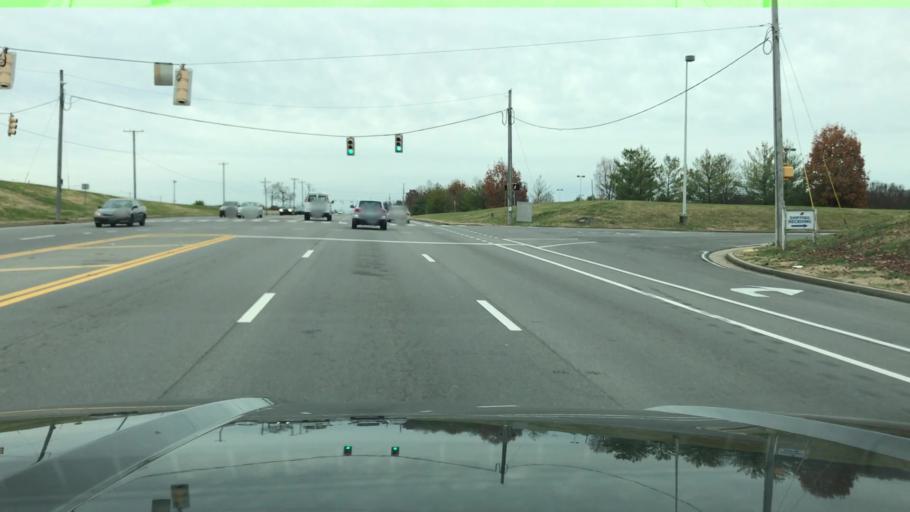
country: US
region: Tennessee
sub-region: Davidson County
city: Oak Hill
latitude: 36.1093
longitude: -86.6806
